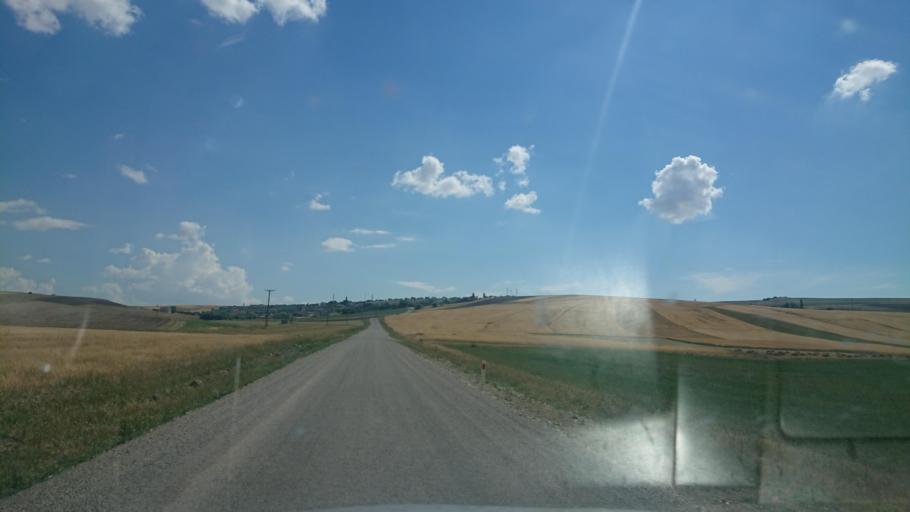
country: TR
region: Aksaray
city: Agacoren
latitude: 38.7823
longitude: 33.7950
